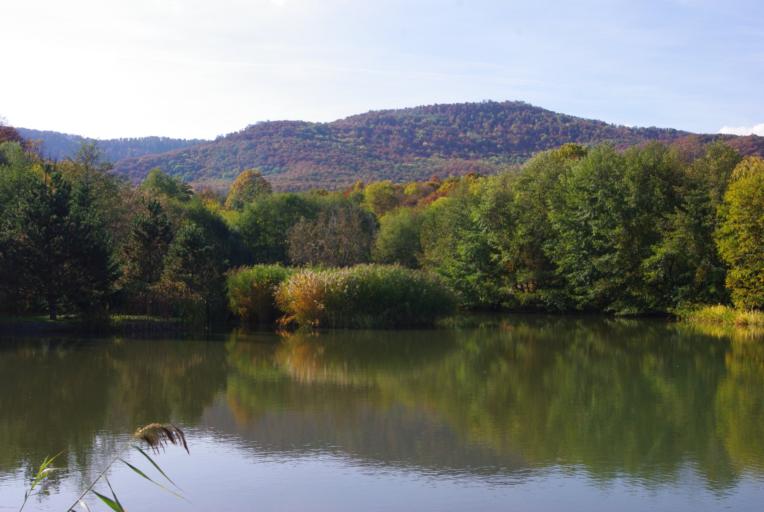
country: HU
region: Pest
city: Dunabogdany
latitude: 47.7635
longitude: 19.0429
